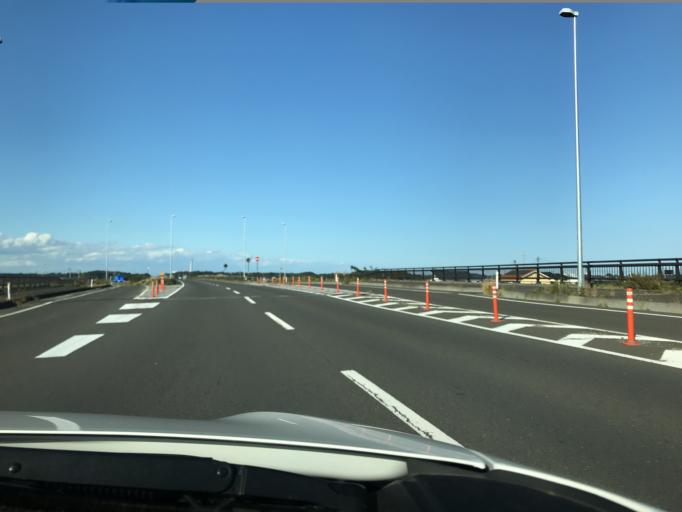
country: JP
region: Miyagi
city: Marumori
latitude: 37.7881
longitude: 140.9440
